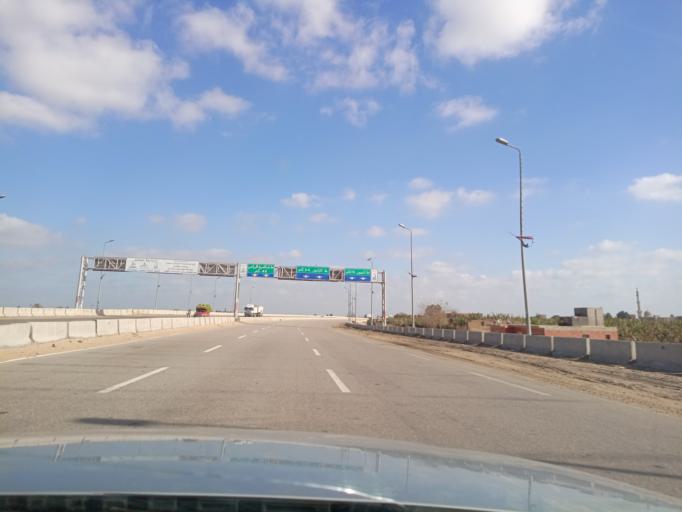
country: EG
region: Muhafazat al Minufiyah
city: Ashmun
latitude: 30.3298
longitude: 30.8356
